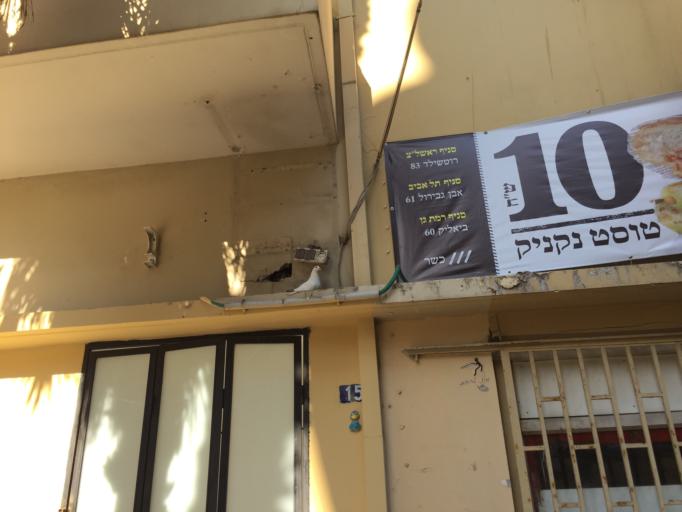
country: IL
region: Tel Aviv
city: Yafo
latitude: 32.0562
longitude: 34.7696
